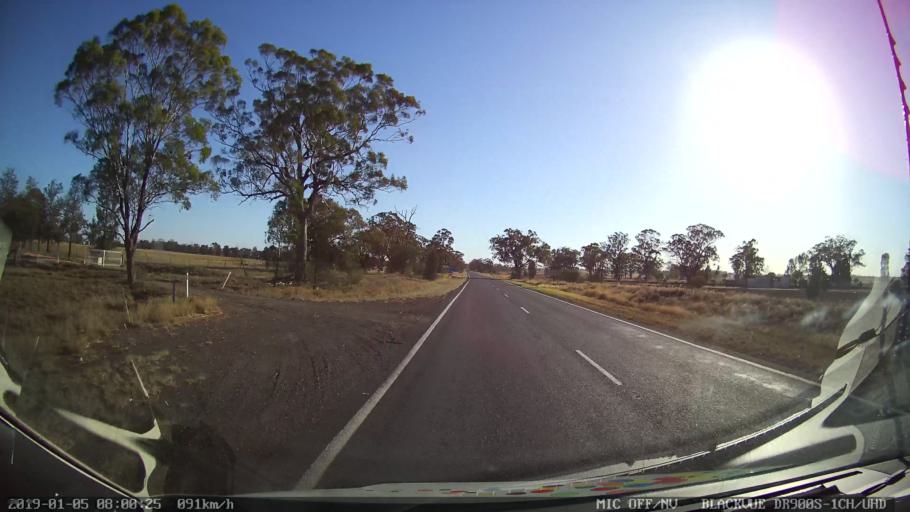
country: AU
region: New South Wales
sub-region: Gilgandra
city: Gilgandra
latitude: -31.6934
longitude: 148.6881
